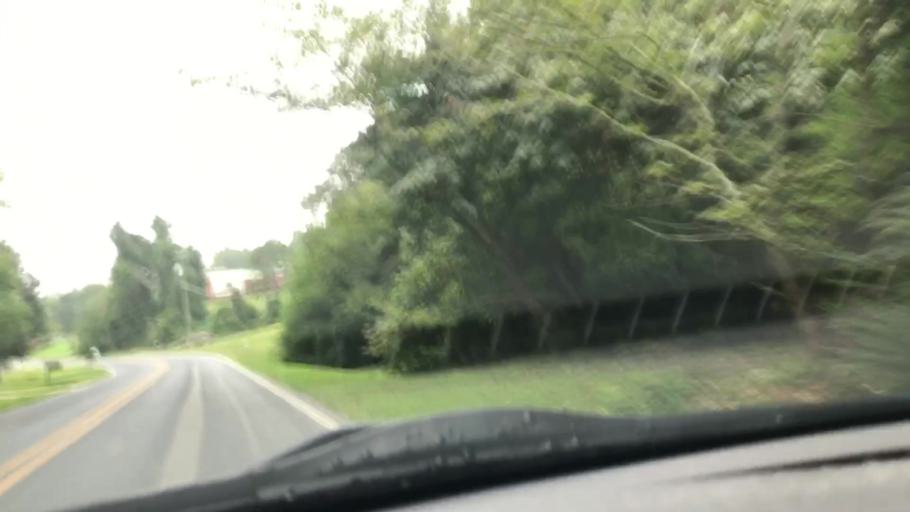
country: US
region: North Carolina
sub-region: Randolph County
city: Asheboro
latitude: 35.7235
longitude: -79.8010
